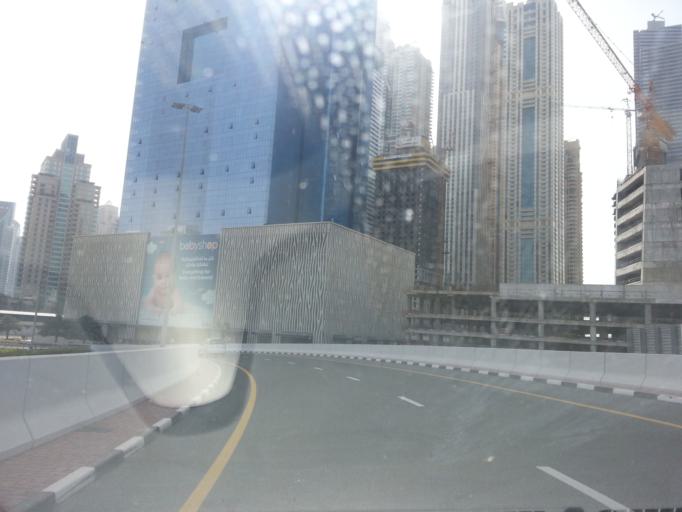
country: AE
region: Dubai
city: Dubai
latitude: 25.0874
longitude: 55.1529
